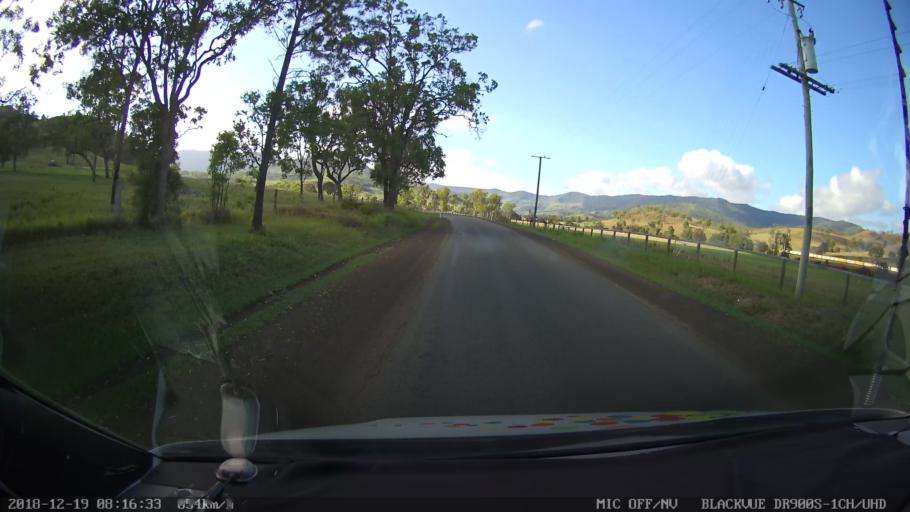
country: AU
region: New South Wales
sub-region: Kyogle
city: Kyogle
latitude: -28.2588
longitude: 152.9066
